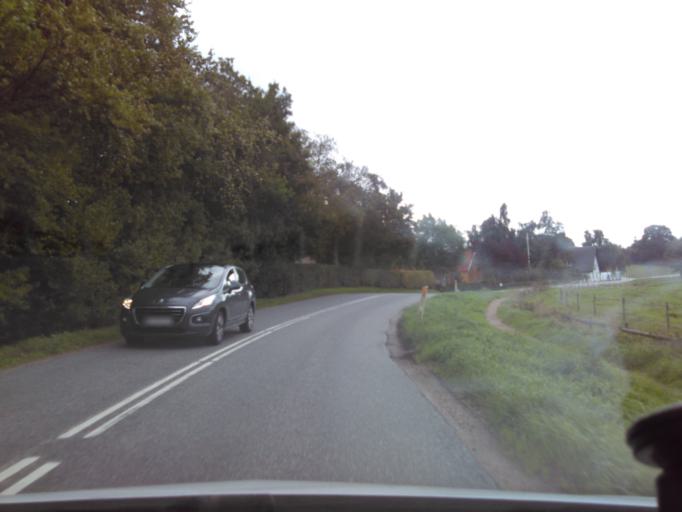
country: DK
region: Capital Region
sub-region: Fureso Kommune
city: Farum
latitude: 55.7955
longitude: 12.3279
